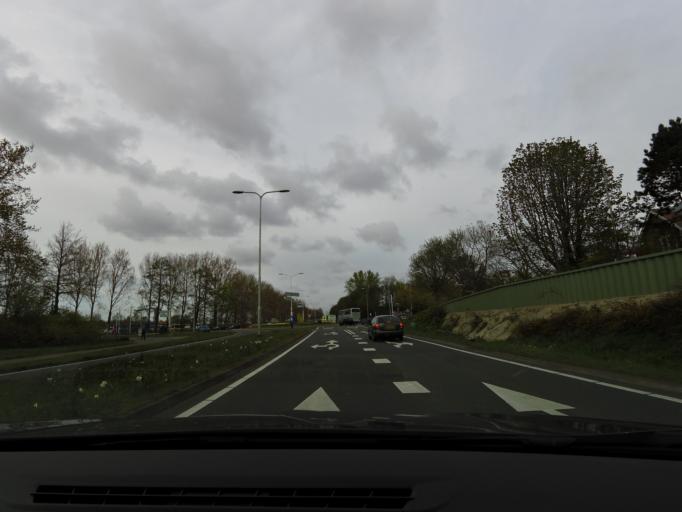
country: NL
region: South Holland
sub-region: Gemeente Lisse
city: Lisse
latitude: 52.2637
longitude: 4.5508
